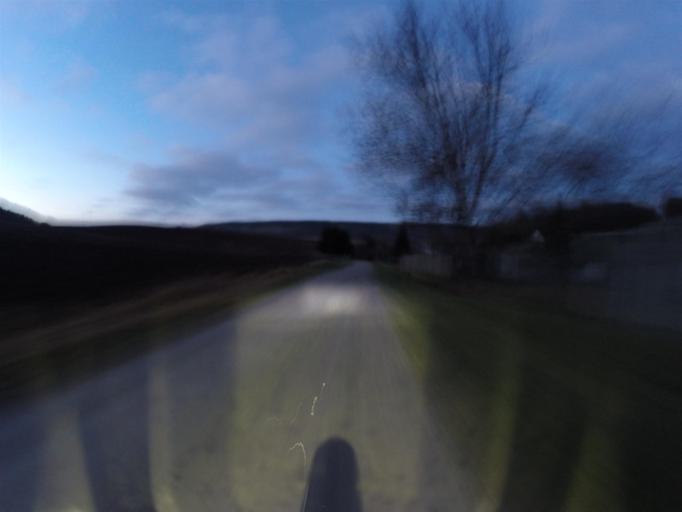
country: DE
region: Thuringia
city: Grosslobichau
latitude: 50.9217
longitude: 11.6492
